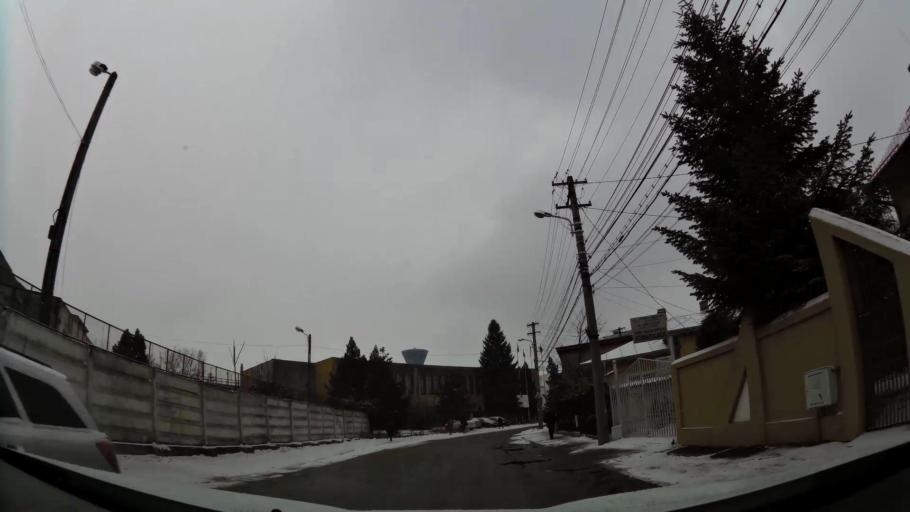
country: RO
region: Prahova
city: Ploiesti
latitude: 44.9254
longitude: 26.0231
